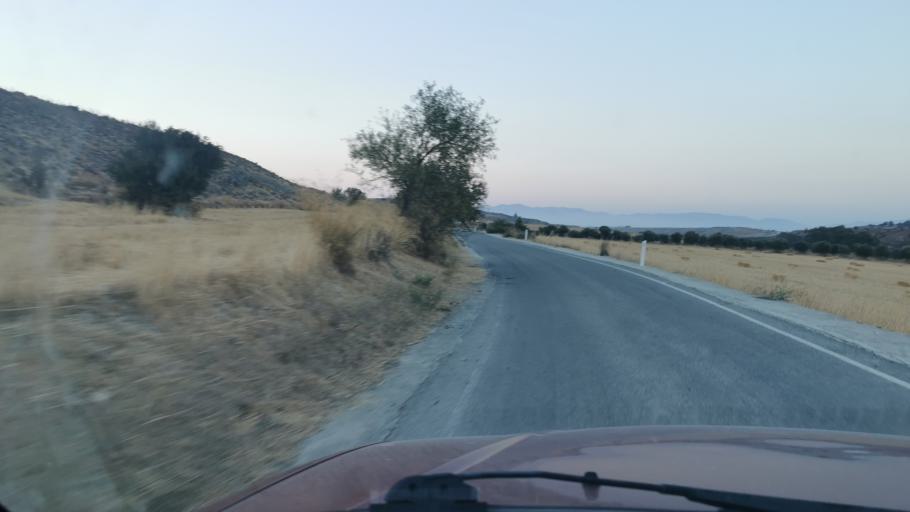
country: CY
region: Lefkosia
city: Peristerona
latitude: 35.0631
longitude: 33.0788
